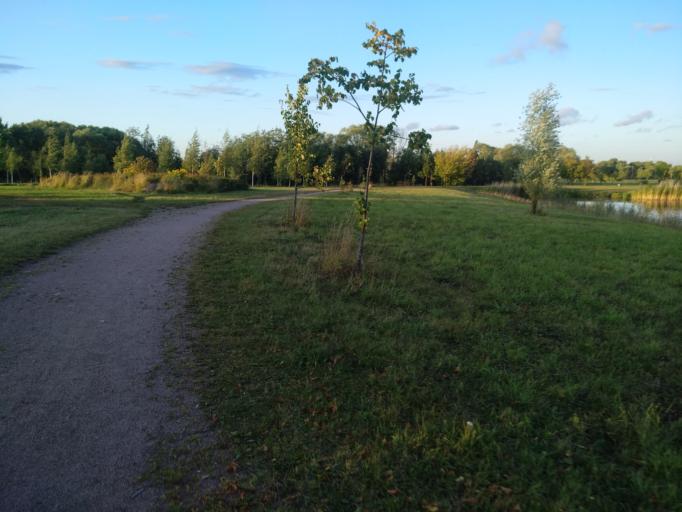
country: RU
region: St.-Petersburg
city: Pushkin
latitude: 59.7447
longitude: 30.3999
